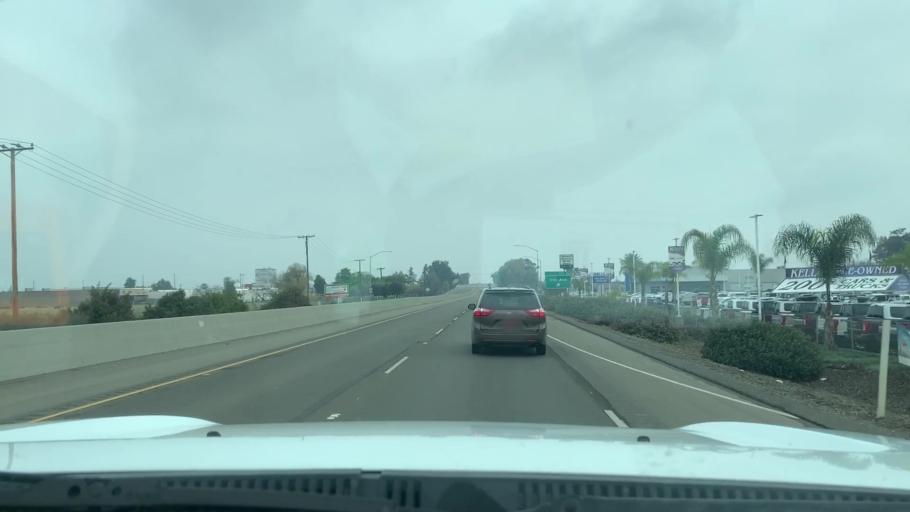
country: US
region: California
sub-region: Kings County
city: Hanford
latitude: 36.3204
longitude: -119.6609
